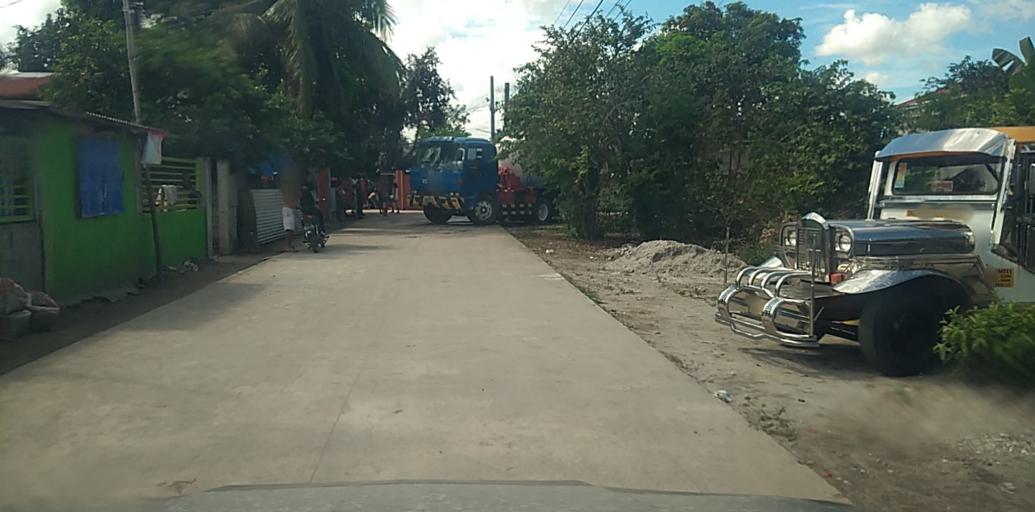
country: PH
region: Central Luzon
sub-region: Province of Pampanga
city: Buensuseso
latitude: 15.1925
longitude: 120.6691
